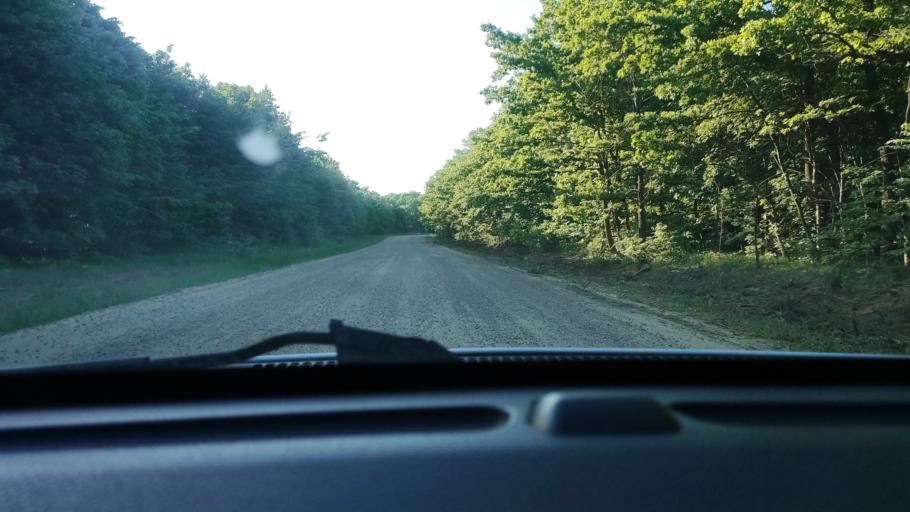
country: RU
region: Krasnodarskiy
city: Novodmitriyevskaya
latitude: 44.7187
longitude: 38.9915
